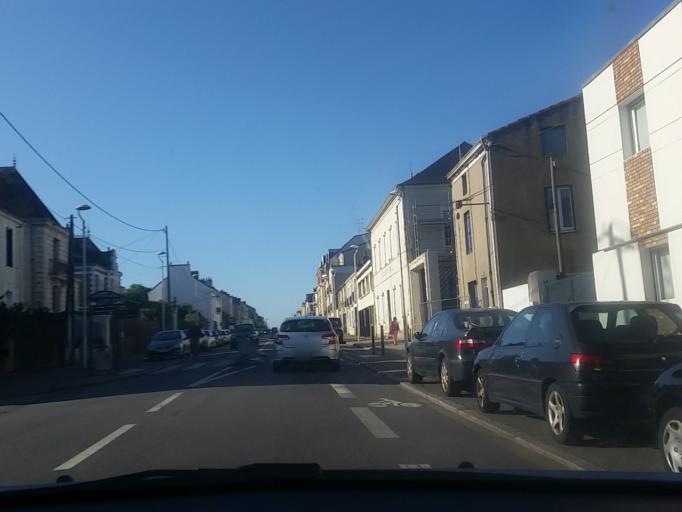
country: FR
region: Pays de la Loire
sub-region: Departement de la Loire-Atlantique
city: Reze
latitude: 47.1872
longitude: -1.5469
